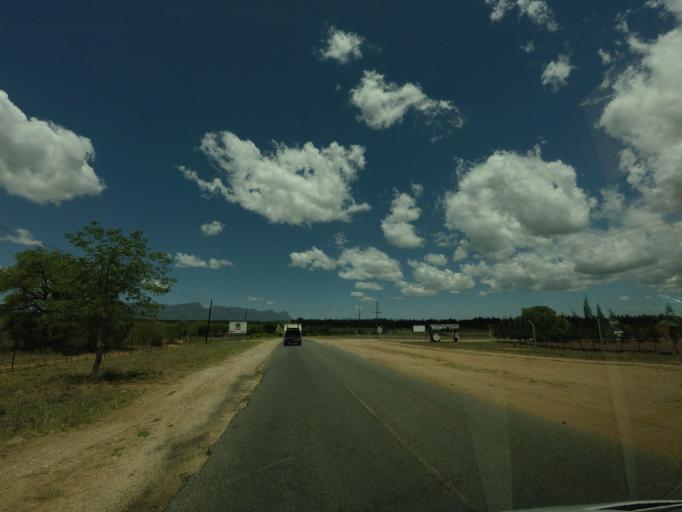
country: ZA
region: Limpopo
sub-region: Mopani District Municipality
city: Hoedspruit
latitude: -24.3701
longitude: 30.9050
